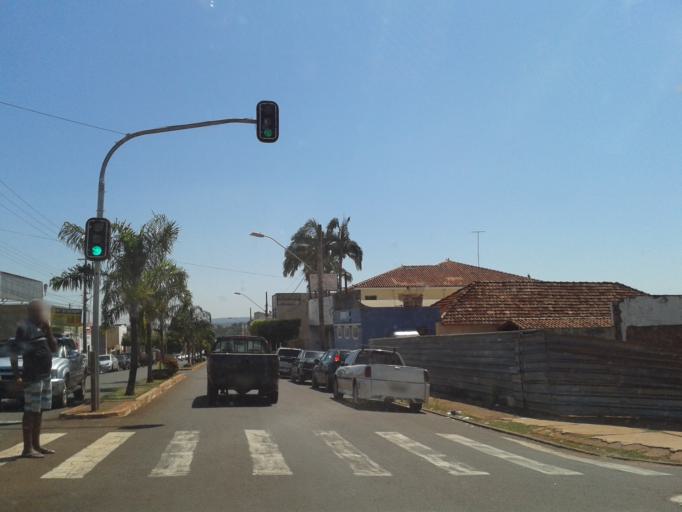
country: BR
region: Minas Gerais
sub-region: Ituiutaba
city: Ituiutaba
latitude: -18.9719
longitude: -49.4608
